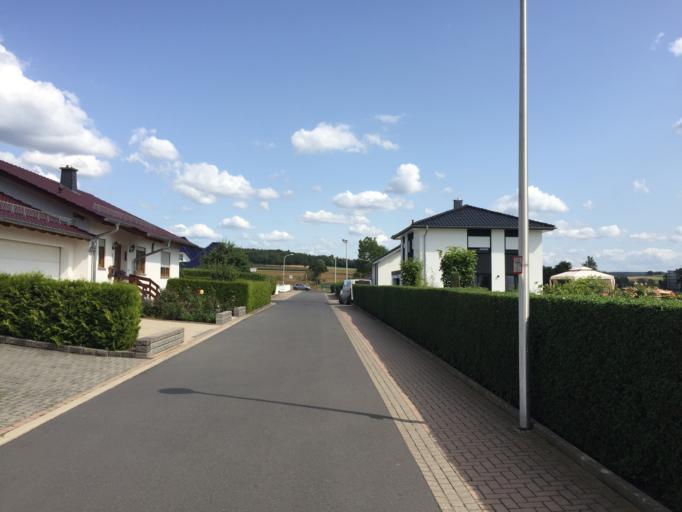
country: DE
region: Hesse
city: Schwalmstadt
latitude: 50.9015
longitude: 9.2746
